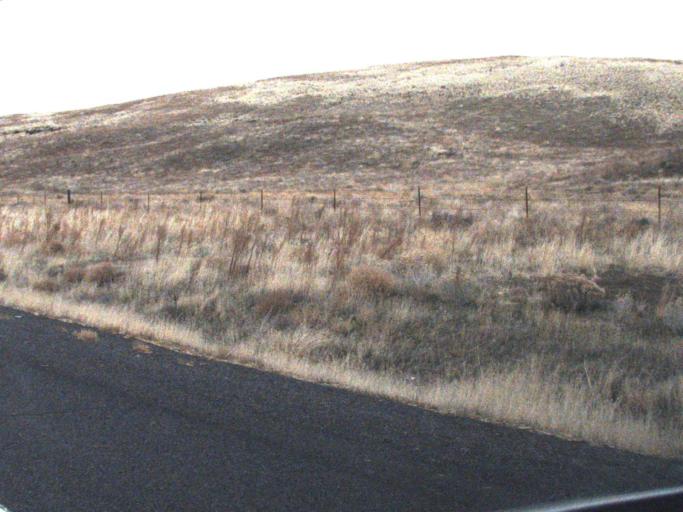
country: US
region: Washington
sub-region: Columbia County
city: Dayton
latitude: 46.7632
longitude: -117.9956
